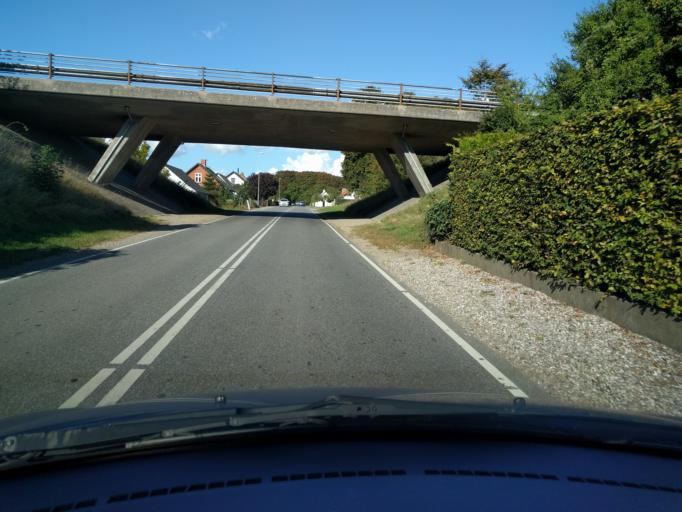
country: DK
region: South Denmark
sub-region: Assens Kommune
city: Assens
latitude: 55.2435
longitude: 9.9833
